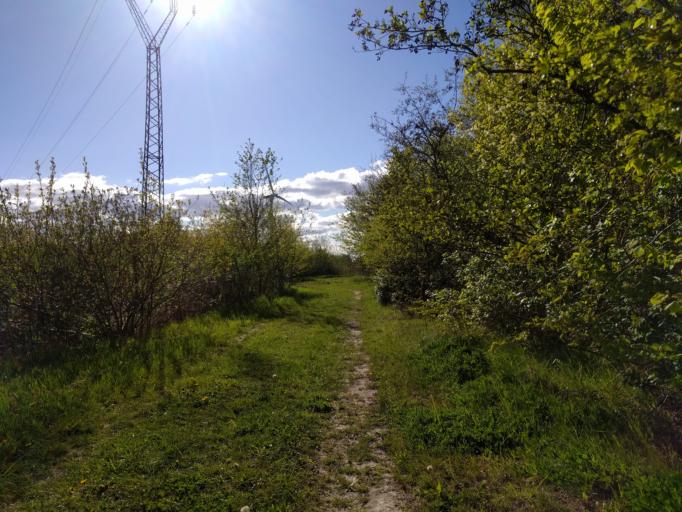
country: DK
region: South Denmark
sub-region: Kerteminde Kommune
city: Munkebo
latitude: 55.4574
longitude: 10.5263
